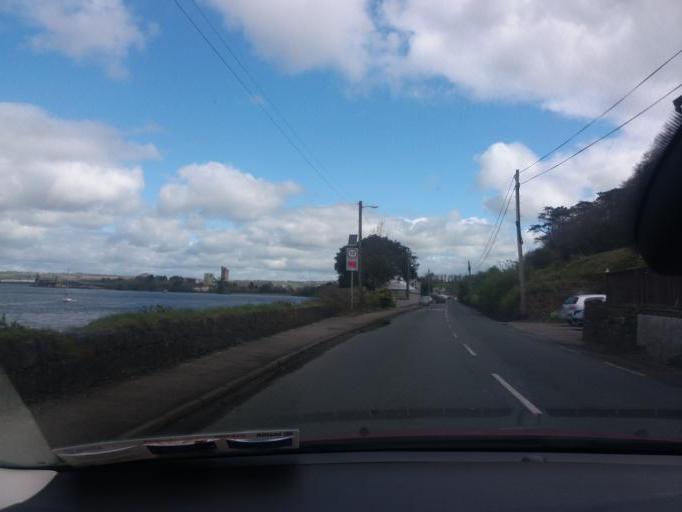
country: IE
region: Munster
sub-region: County Cork
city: Passage West
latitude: 51.8667
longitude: -8.3254
